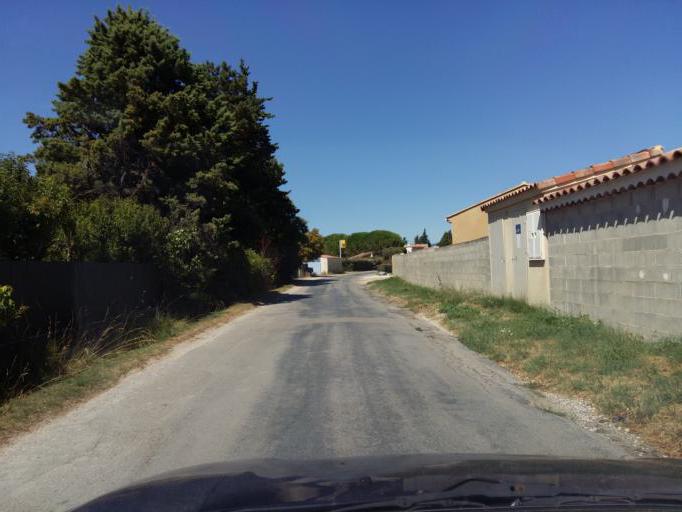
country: FR
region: Provence-Alpes-Cote d'Azur
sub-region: Departement du Vaucluse
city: Loriol-du-Comtat
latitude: 44.0802
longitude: 5.0045
